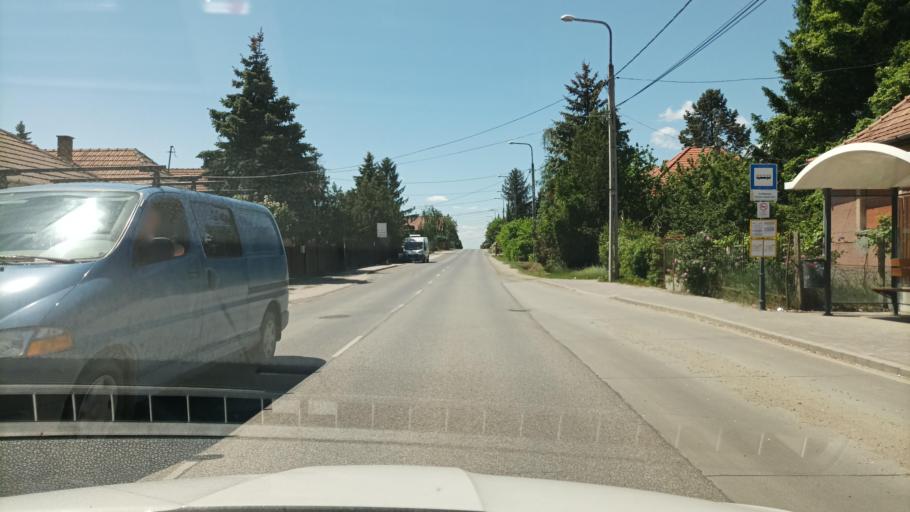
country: HU
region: Pest
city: Erdokertes
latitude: 47.6738
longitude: 19.3137
